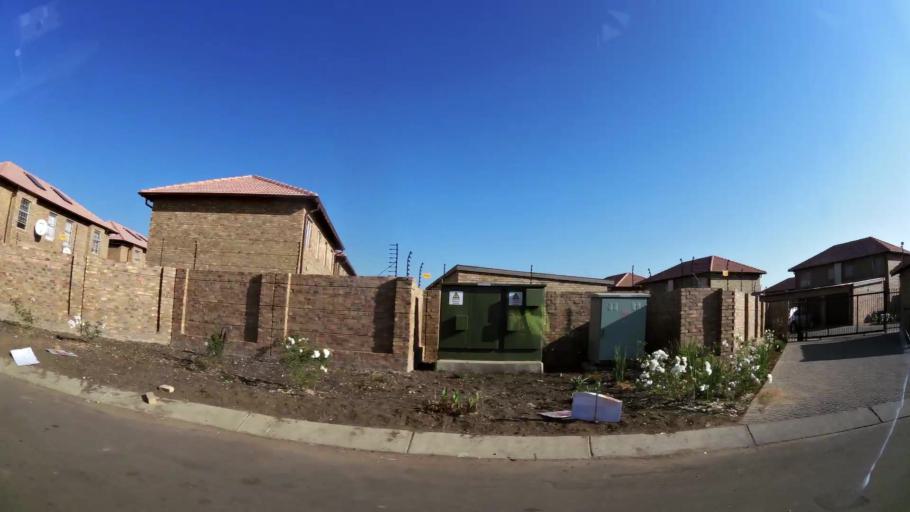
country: ZA
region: Gauteng
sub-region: City of Tshwane Metropolitan Municipality
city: Pretoria
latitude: -25.6676
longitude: 28.2171
